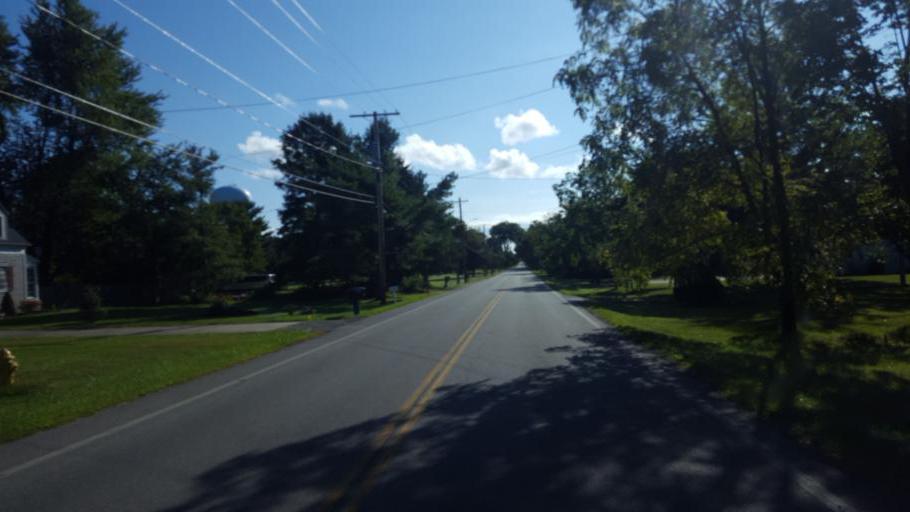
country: US
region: Ohio
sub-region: Lorain County
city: Oberlin
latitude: 41.2943
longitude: -82.2350
